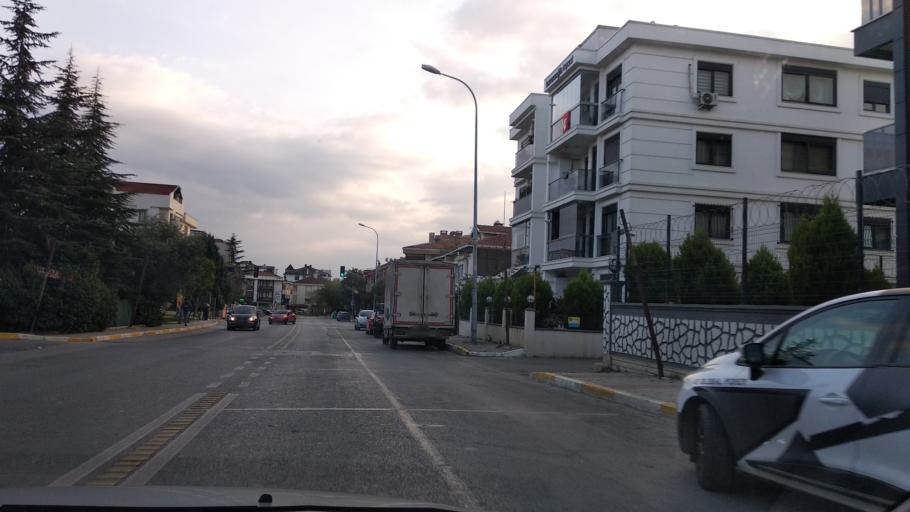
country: TR
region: Istanbul
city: Icmeler
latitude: 40.8216
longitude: 29.2997
